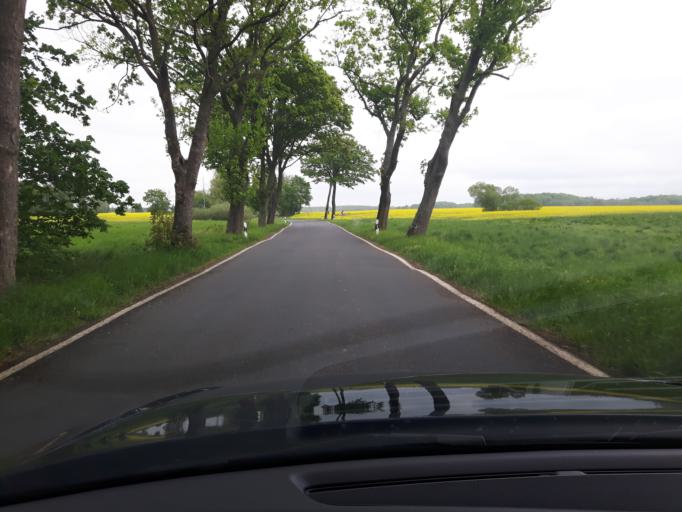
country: DE
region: Mecklenburg-Vorpommern
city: Velgast
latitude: 54.2044
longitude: 12.7307
